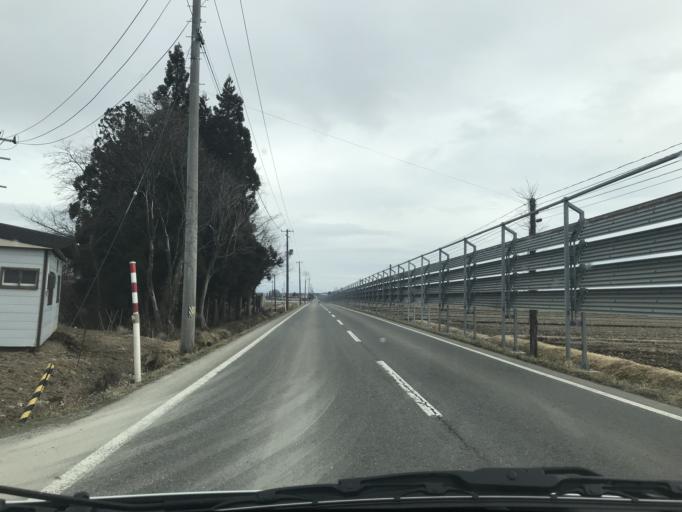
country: JP
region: Iwate
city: Kitakami
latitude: 39.3127
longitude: 141.0214
